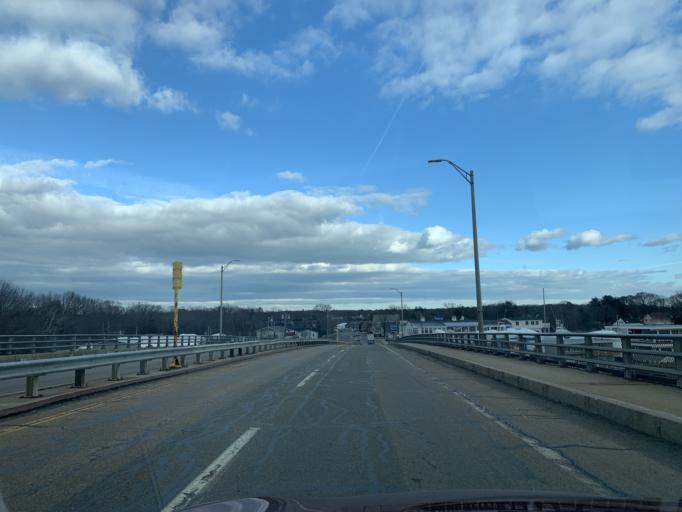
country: US
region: Massachusetts
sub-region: Essex County
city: Newburyport
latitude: 42.8163
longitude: -70.8723
